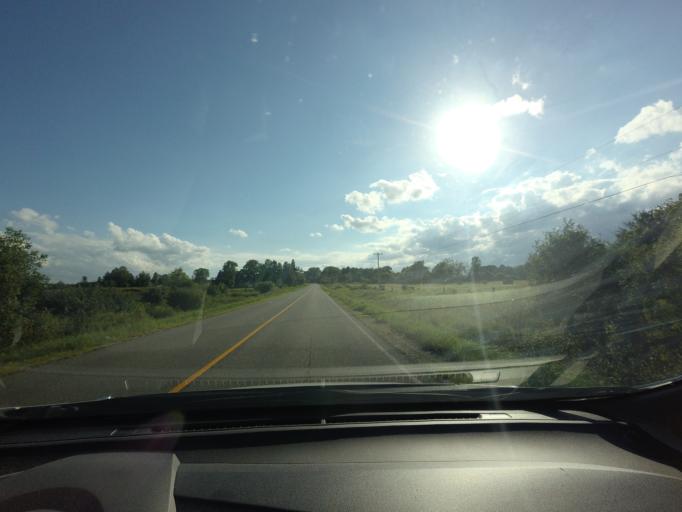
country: CA
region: Ontario
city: Perth
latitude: 44.9086
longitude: -76.2278
